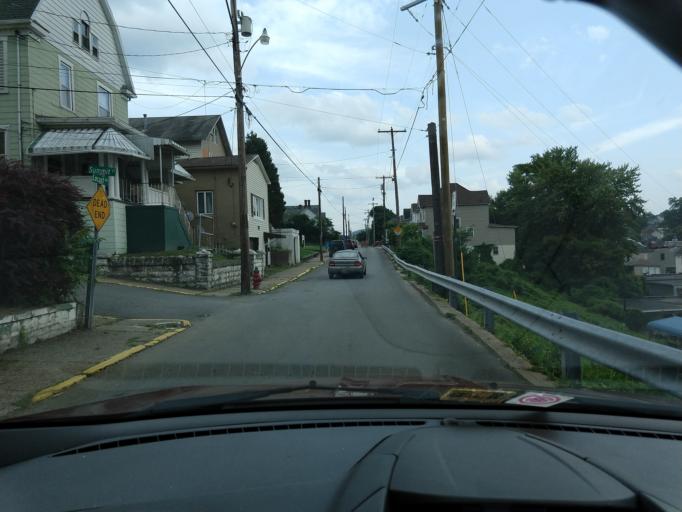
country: US
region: West Virginia
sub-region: Harrison County
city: Clarksburg
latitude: 39.2834
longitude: -80.3498
